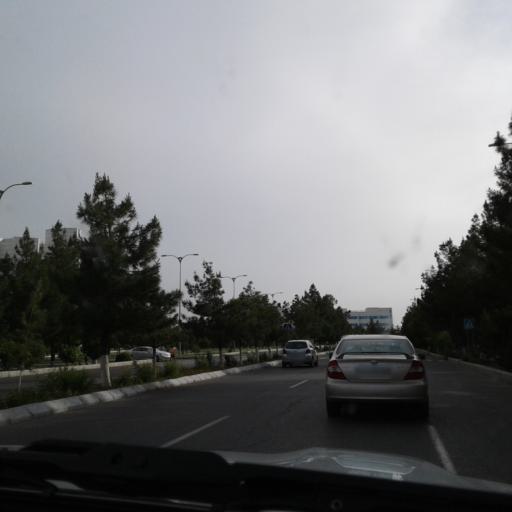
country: TM
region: Mary
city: Mary
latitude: 37.5861
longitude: 61.8617
